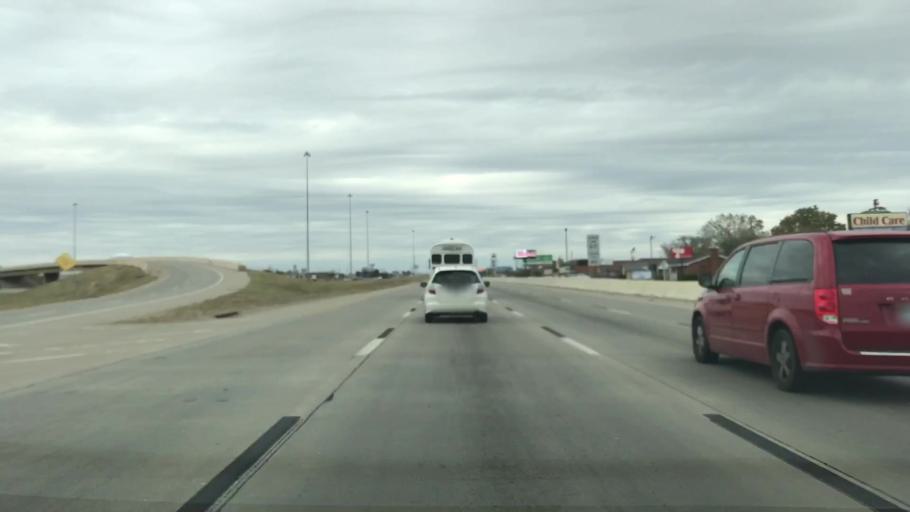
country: US
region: Oklahoma
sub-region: Cleveland County
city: Moore
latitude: 35.3552
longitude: -97.4946
